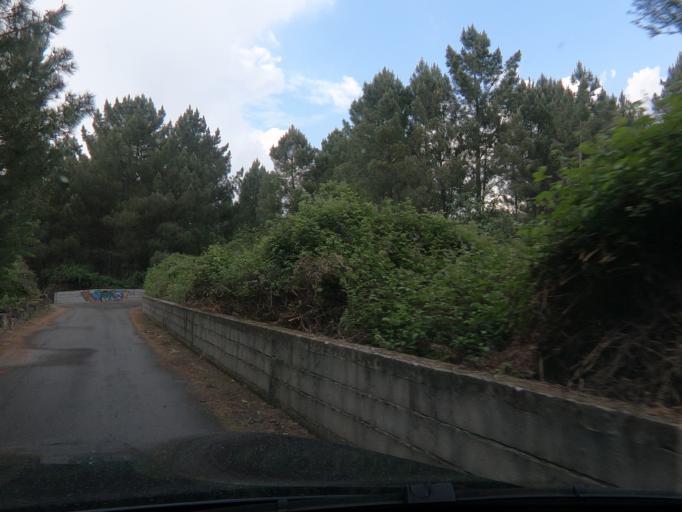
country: PT
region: Vila Real
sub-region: Vila Real
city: Vila Real
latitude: 41.3091
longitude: -7.7120
